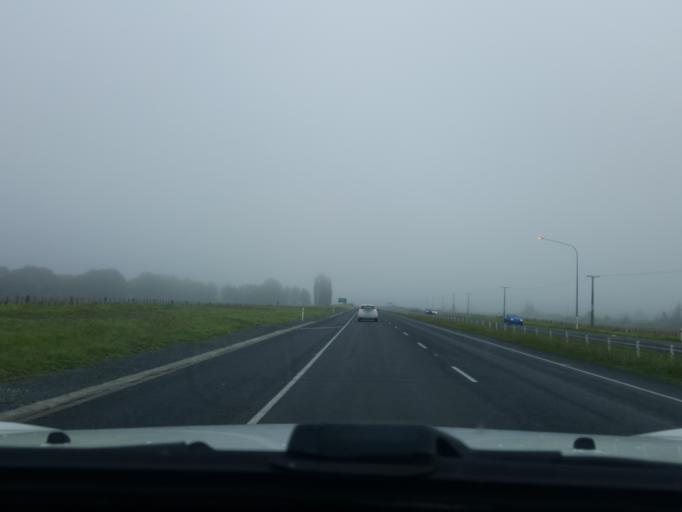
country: NZ
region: Waikato
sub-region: Waikato District
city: Te Kauwhata
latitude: -37.4390
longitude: 175.1466
